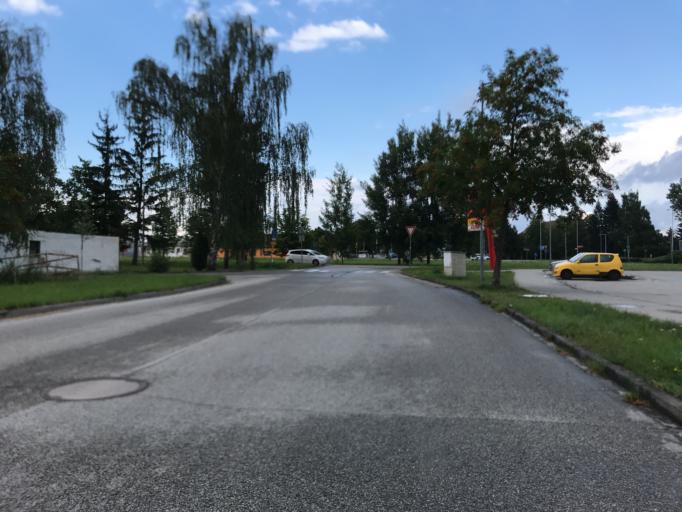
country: CZ
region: Jihocesky
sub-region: Okres Jindrichuv Hradec
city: Trebon
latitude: 49.0123
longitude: 14.7550
